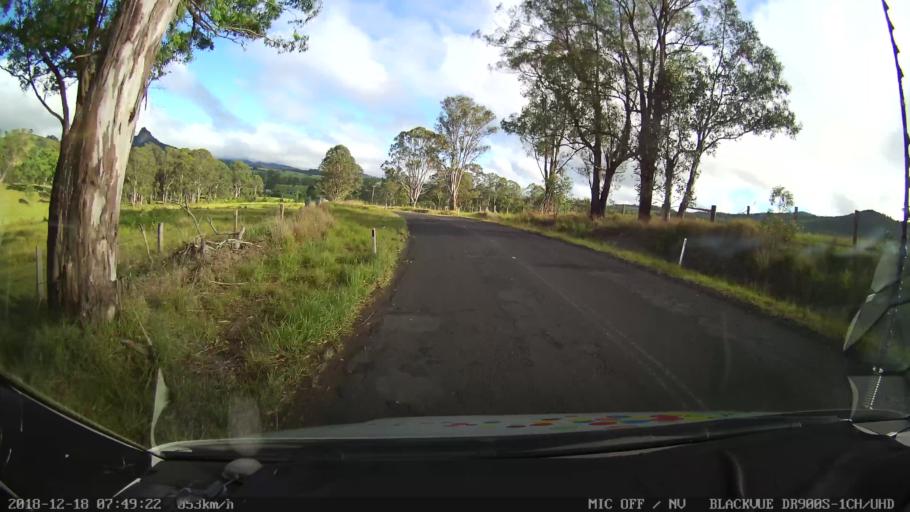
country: AU
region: New South Wales
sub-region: Kyogle
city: Kyogle
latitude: -28.4543
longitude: 152.5704
